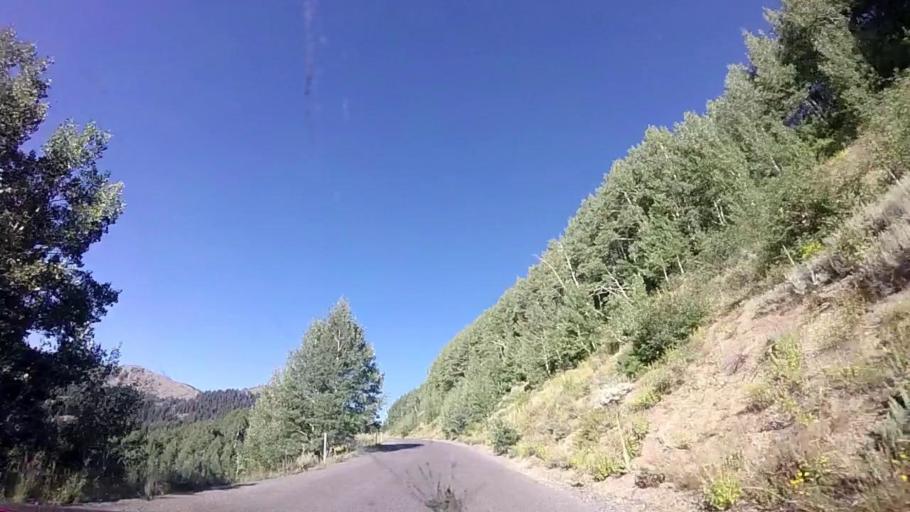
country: US
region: Utah
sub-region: Summit County
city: Park City
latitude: 40.6098
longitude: -111.5421
